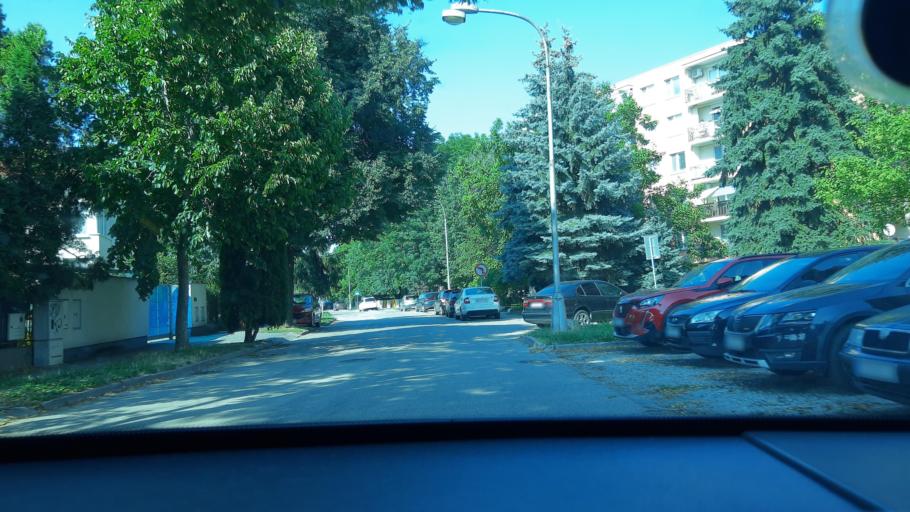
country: SK
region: Trnavsky
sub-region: Okres Trnava
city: Piestany
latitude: 48.6004
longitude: 17.8363
